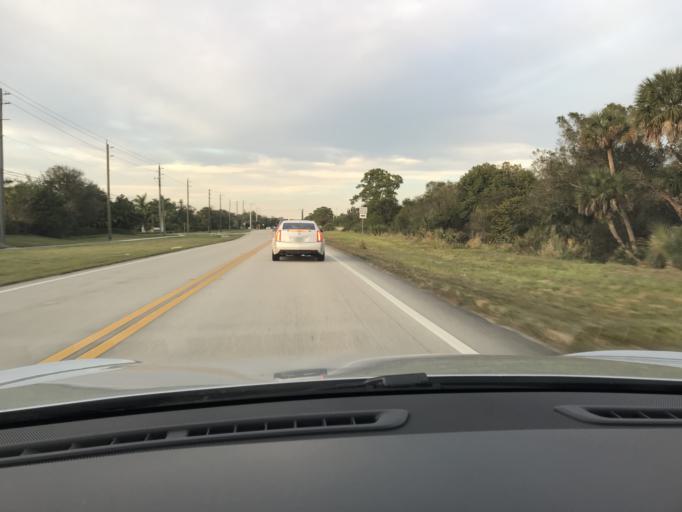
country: US
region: Florida
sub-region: Indian River County
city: Vero Beach South
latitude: 27.5840
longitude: -80.4307
